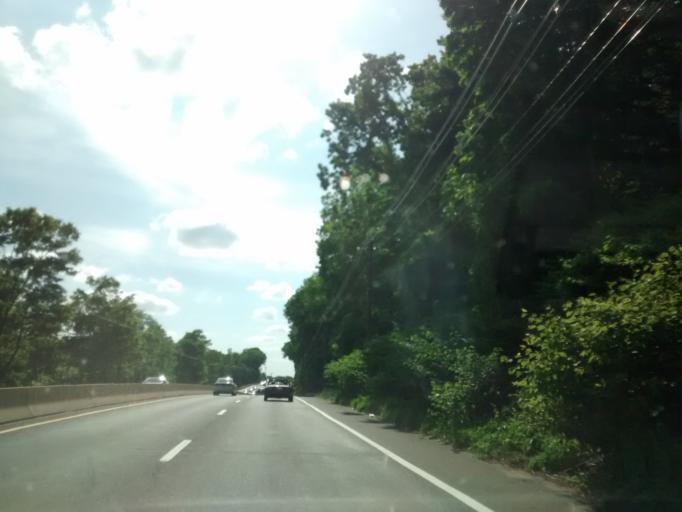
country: US
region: Massachusetts
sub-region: Worcester County
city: Shrewsbury
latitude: 42.2770
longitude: -71.7003
